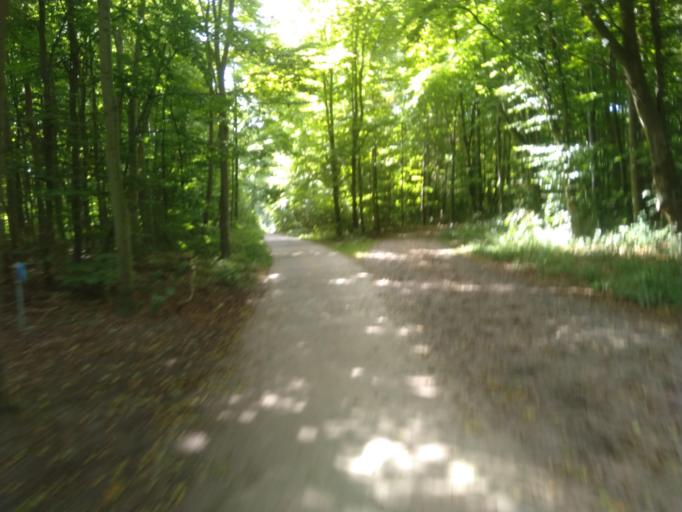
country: NL
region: North Holland
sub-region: Gemeente Zaanstad
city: Zaanstad
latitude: 52.3961
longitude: 4.7411
